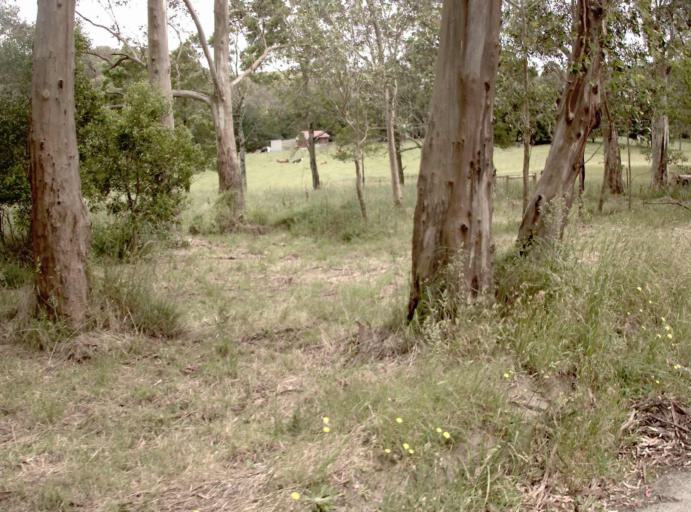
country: AU
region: Victoria
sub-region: Latrobe
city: Moe
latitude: -37.9901
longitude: 146.1454
